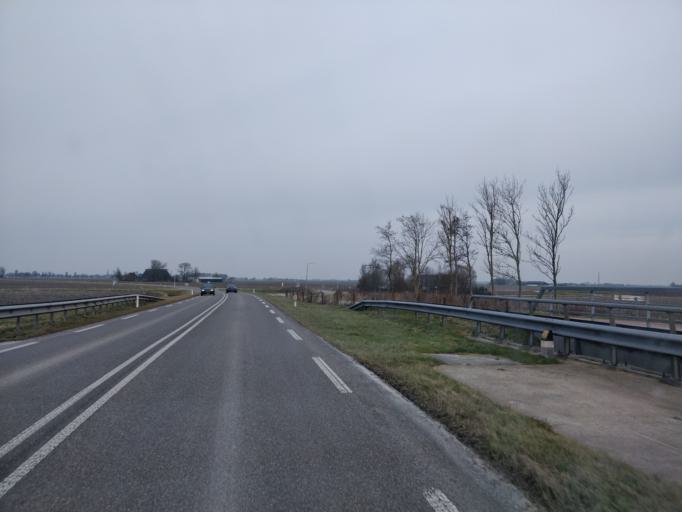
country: NL
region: Friesland
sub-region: Gemeente Leeuwarderadeel
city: Stiens
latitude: 53.2800
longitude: 5.7639
